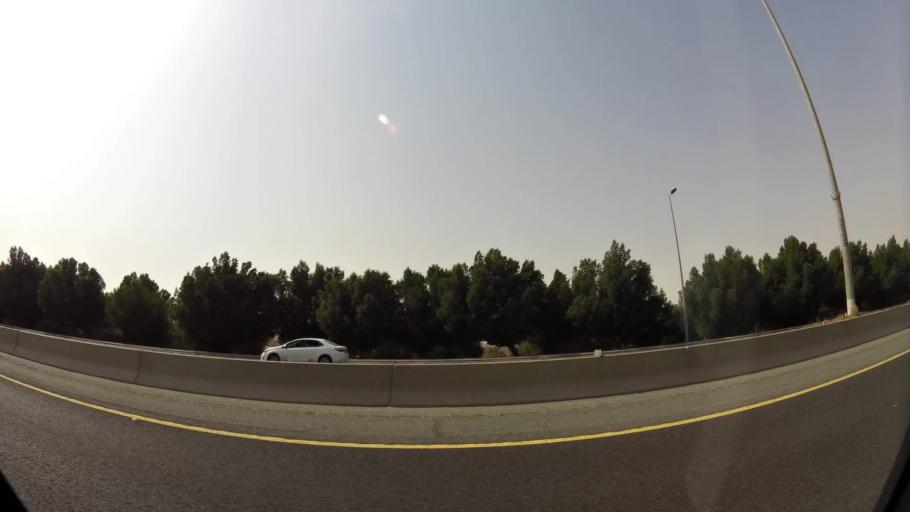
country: KW
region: Muhafazat al Jahra'
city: Al Jahra'
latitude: 29.3590
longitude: 47.6752
